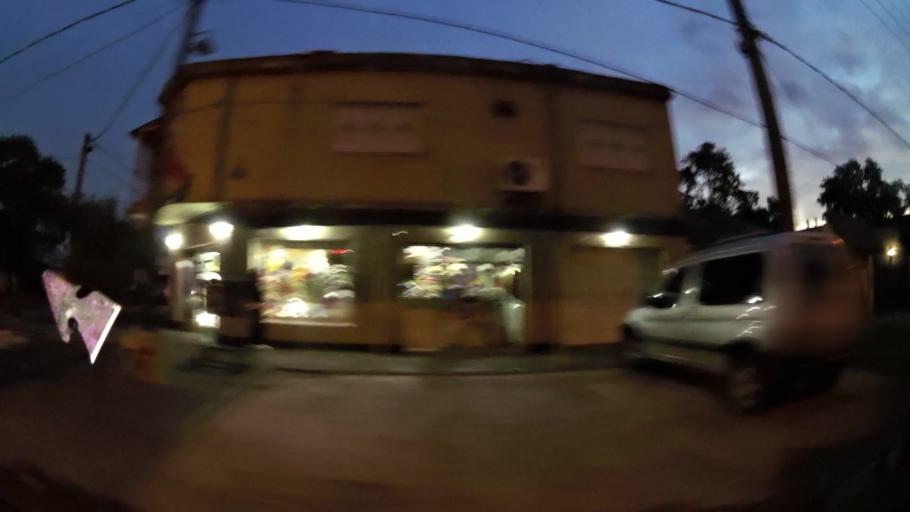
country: AR
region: Buenos Aires
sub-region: Partido de Lanus
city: Lanus
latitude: -34.7400
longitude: -58.3540
